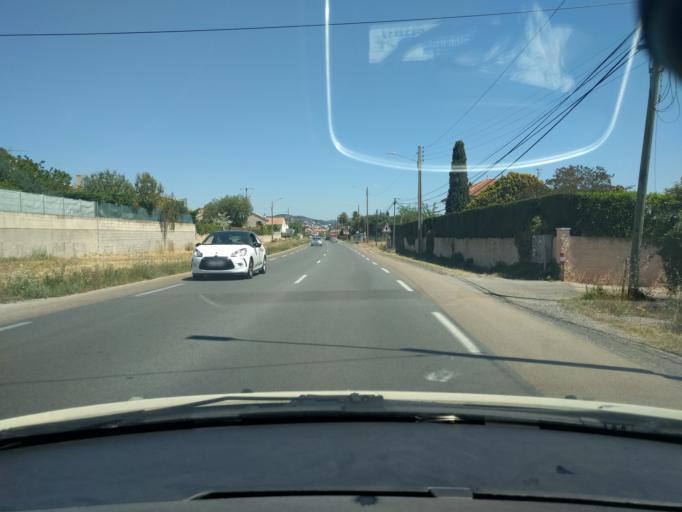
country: FR
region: Provence-Alpes-Cote d'Azur
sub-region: Departement du Var
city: Hyeres
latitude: 43.0928
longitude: 6.1302
